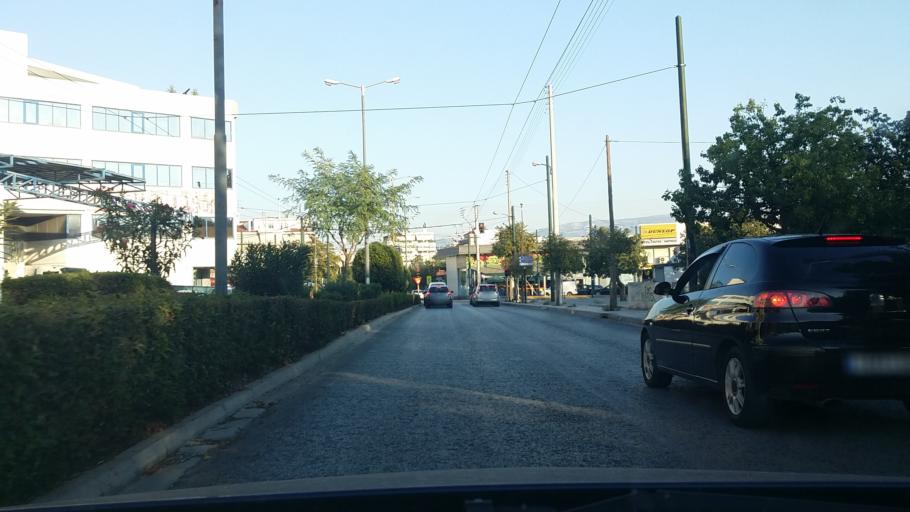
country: GR
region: Attica
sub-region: Nomarchia Athinas
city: Ilion
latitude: 38.0281
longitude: 23.6972
